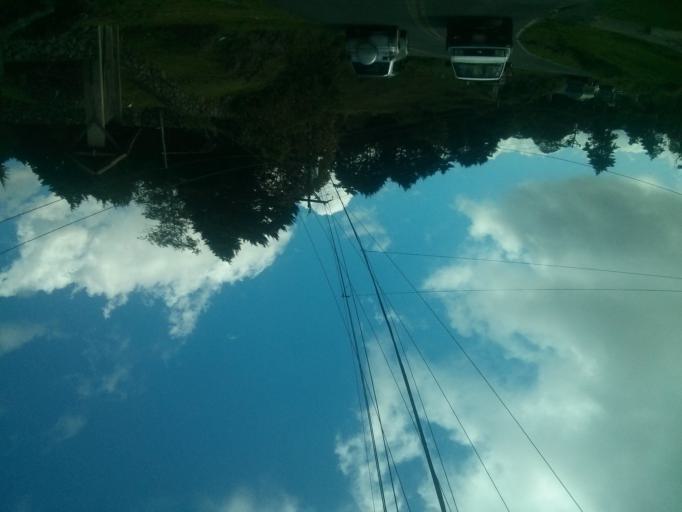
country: CR
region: Cartago
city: Cot
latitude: 9.8905
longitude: -83.8544
